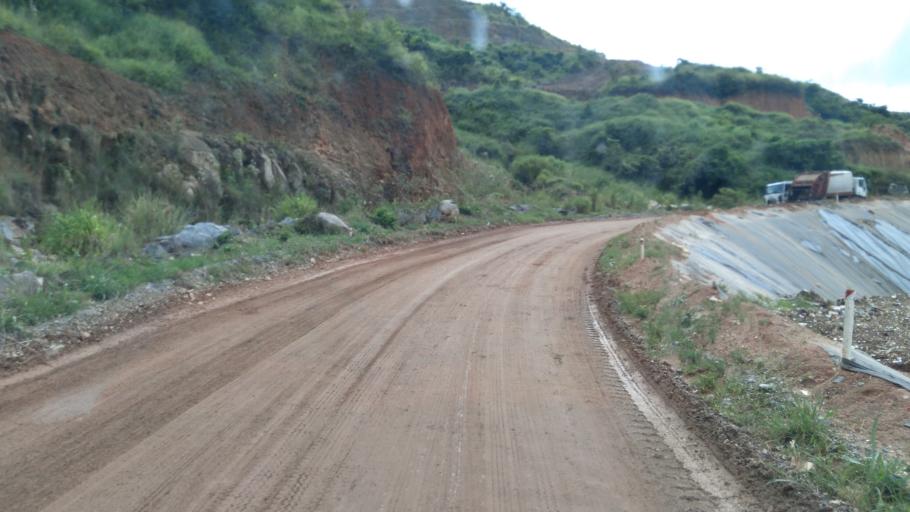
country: BR
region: Minas Gerais
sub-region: Santa Luzia
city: Santa Luzia
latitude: -19.8504
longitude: -43.8479
